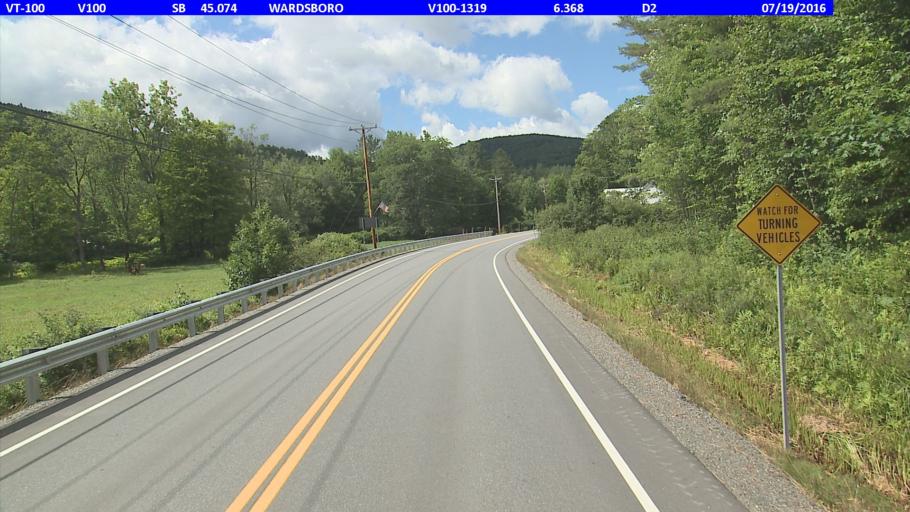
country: US
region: Vermont
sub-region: Windham County
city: Dover
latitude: 43.0906
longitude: -72.8676
